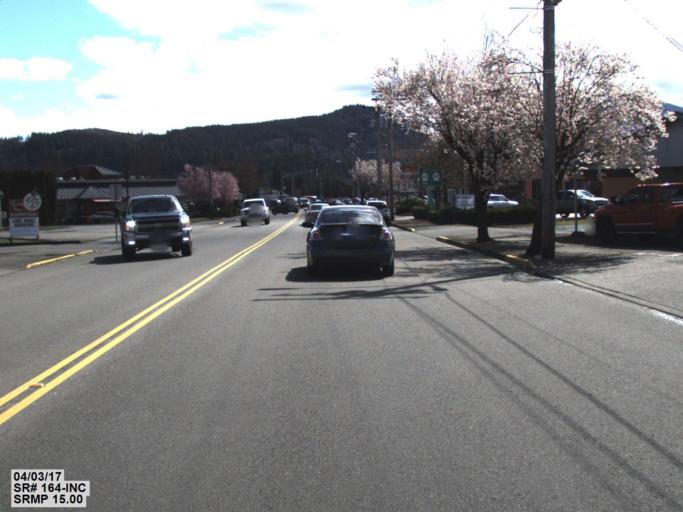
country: US
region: Washington
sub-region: King County
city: Enumclaw
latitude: 47.2005
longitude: -121.9833
